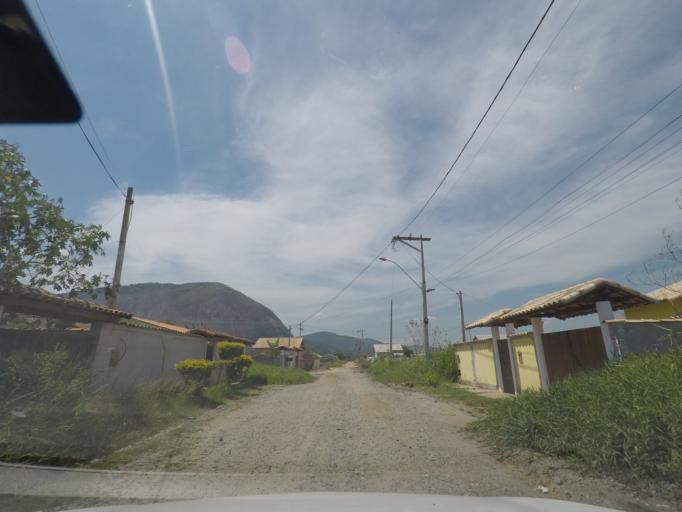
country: BR
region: Rio de Janeiro
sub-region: Marica
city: Marica
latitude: -22.9526
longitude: -42.9550
